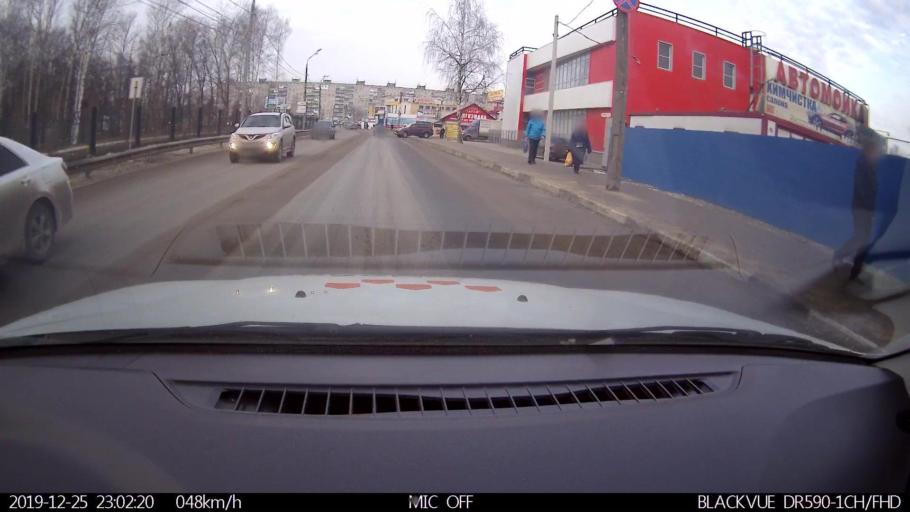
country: RU
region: Nizjnij Novgorod
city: Gorbatovka
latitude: 56.3583
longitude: 43.8273
